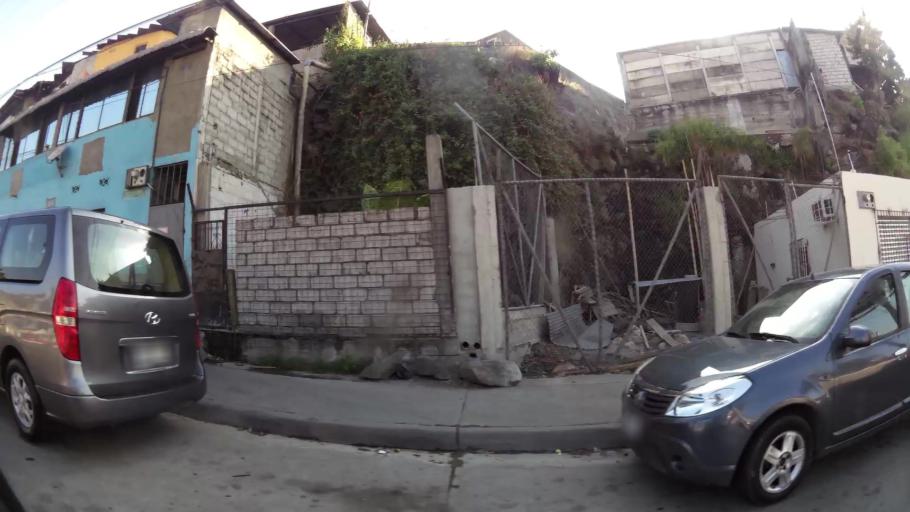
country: EC
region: Guayas
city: Guayaquil
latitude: -2.1555
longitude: -79.9132
